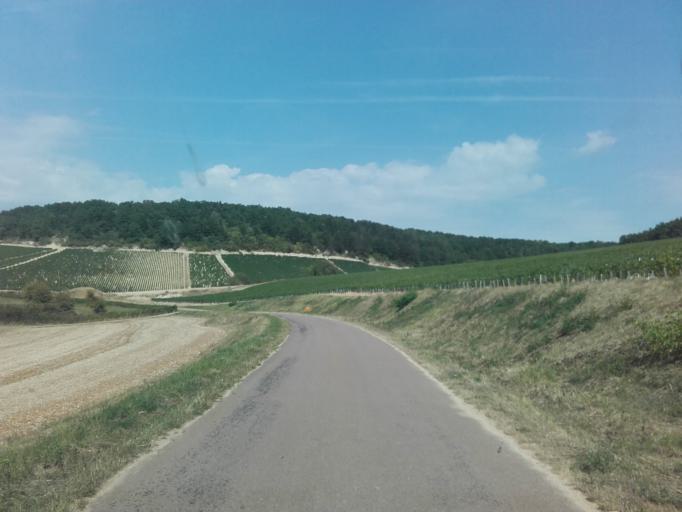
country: FR
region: Bourgogne
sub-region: Departement de l'Yonne
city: Chablis
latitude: 47.8244
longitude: 3.8590
